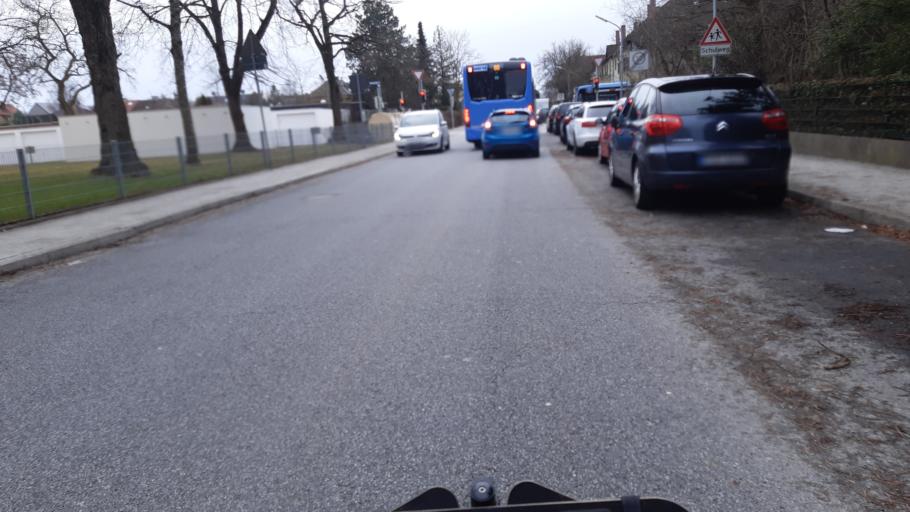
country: DE
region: Bavaria
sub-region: Upper Bavaria
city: Oberschleissheim
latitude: 48.2089
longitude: 11.5560
